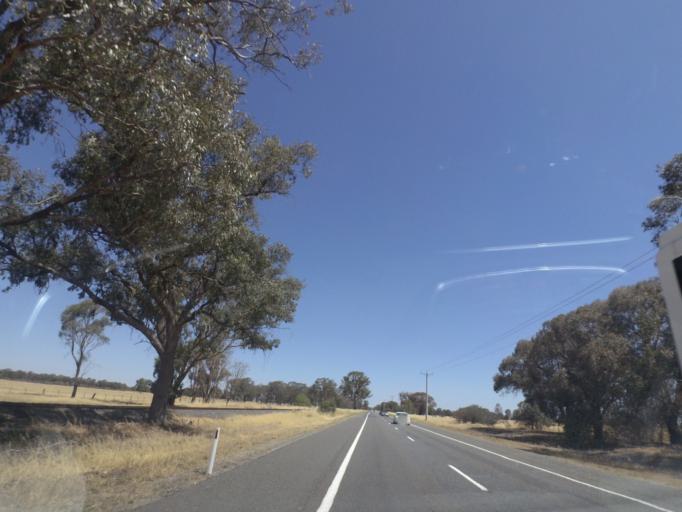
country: AU
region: Victoria
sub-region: Greater Shepparton
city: Shepparton
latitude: -36.2075
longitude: 145.4319
